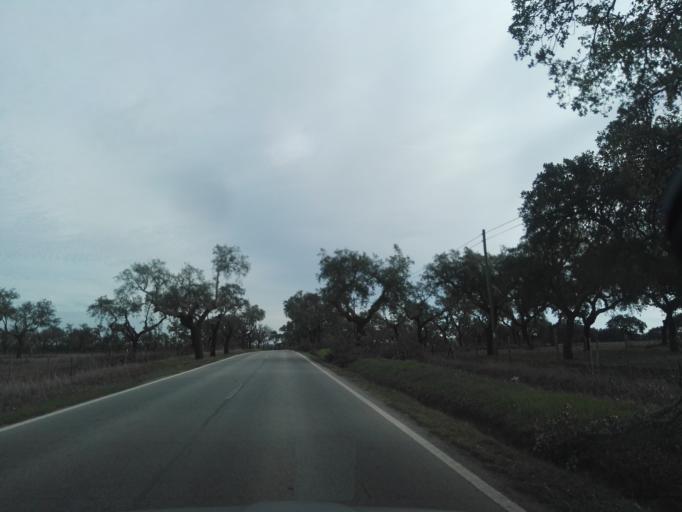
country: PT
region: Portalegre
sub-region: Elvas
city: Elvas
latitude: 38.9356
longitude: -7.1911
